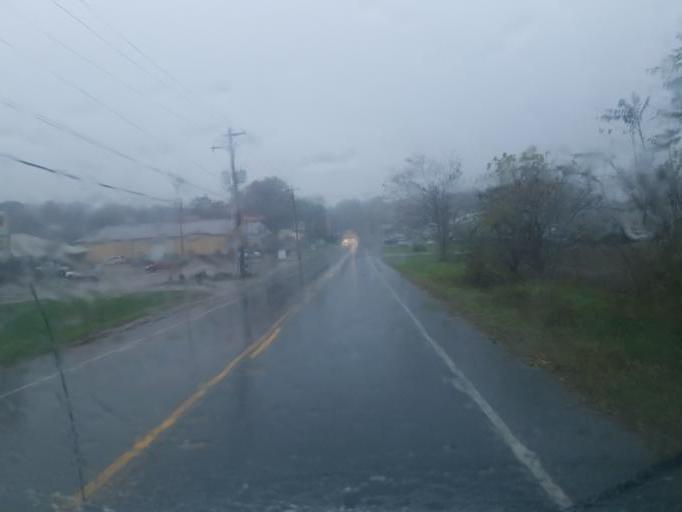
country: US
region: Ohio
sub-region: Muskingum County
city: Zanesville
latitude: 39.9568
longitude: -82.0247
